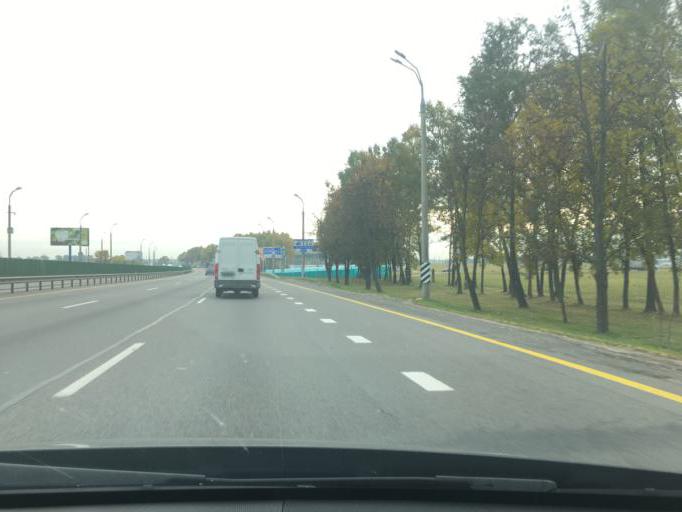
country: BY
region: Minsk
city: Malinovka
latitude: 53.8562
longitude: 27.4297
